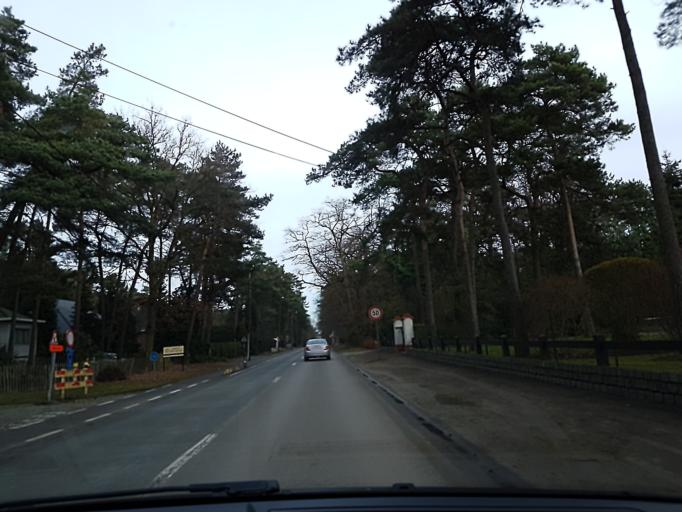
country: BE
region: Flanders
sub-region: Provincie Vlaams-Brabant
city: Boortmeerbeek
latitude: 51.0063
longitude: 4.5918
